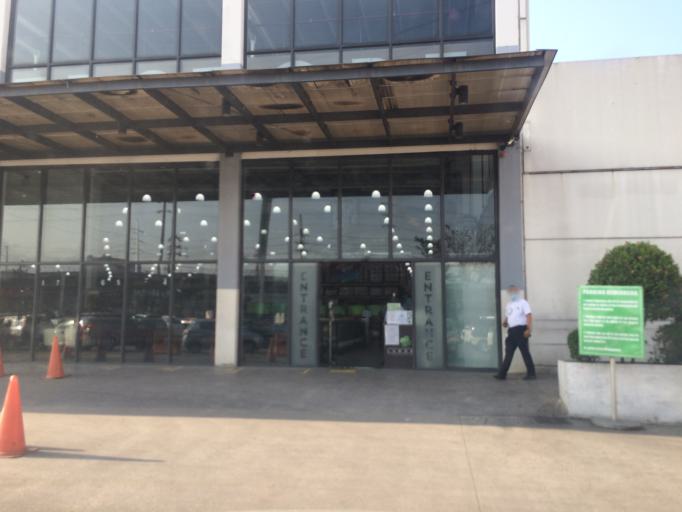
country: PH
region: Calabarzon
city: Del Monte
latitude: 14.6583
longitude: 121.0125
